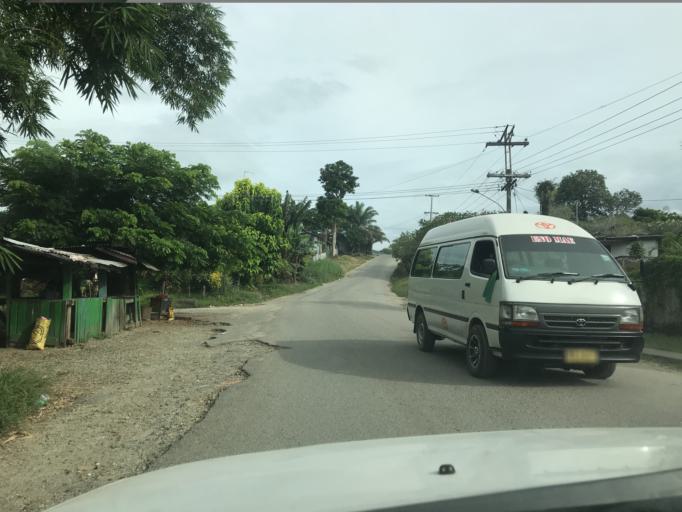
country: SB
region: Guadalcanal
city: Honiara
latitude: -9.4351
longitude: 159.9451
